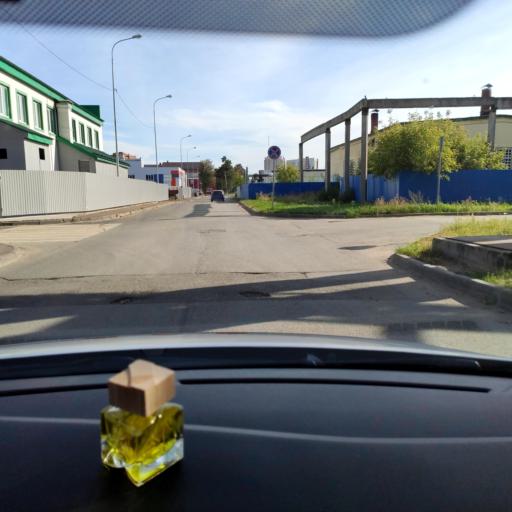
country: RU
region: Tatarstan
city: Staroye Arakchino
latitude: 55.8366
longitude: 49.0492
